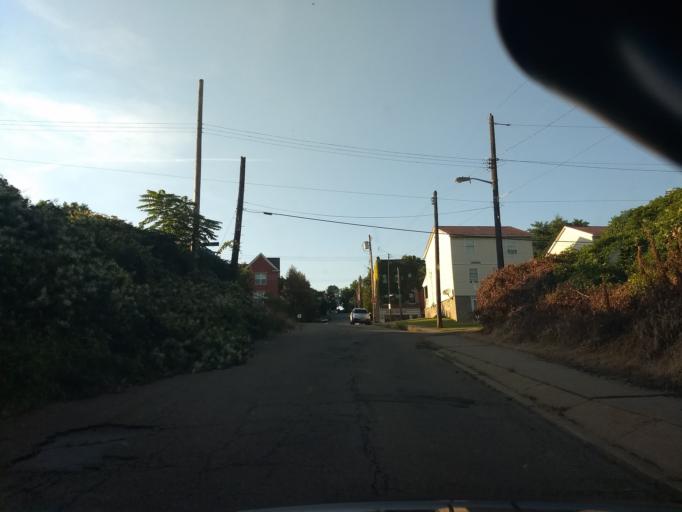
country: US
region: Pennsylvania
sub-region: Allegheny County
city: Pittsburgh
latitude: 40.4469
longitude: -79.9730
